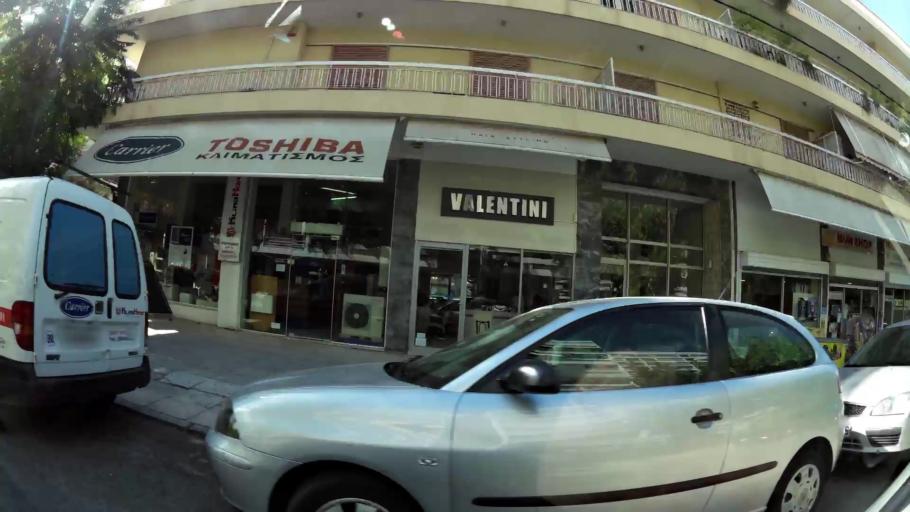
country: GR
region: Attica
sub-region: Nomarchia Athinas
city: Neo Psychiko
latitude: 38.0034
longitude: 23.7903
